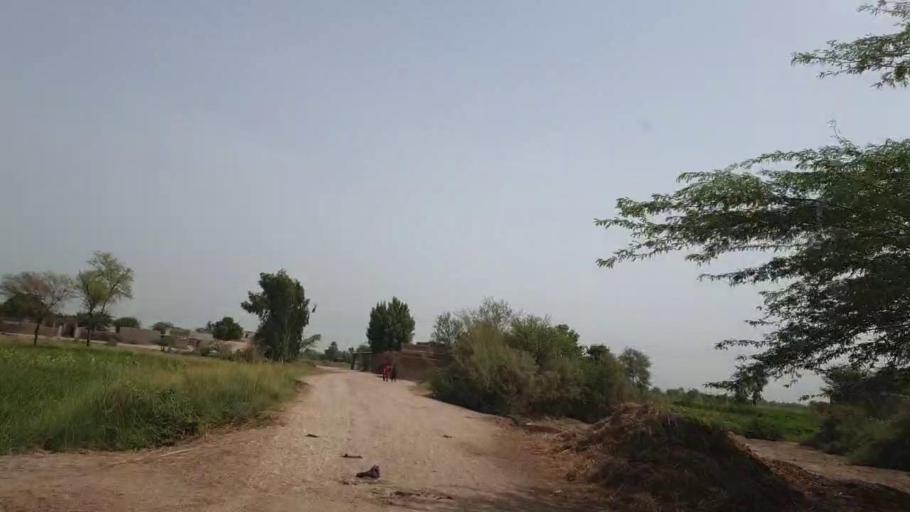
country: PK
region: Sindh
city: Sakrand
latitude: 26.1225
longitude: 68.3697
